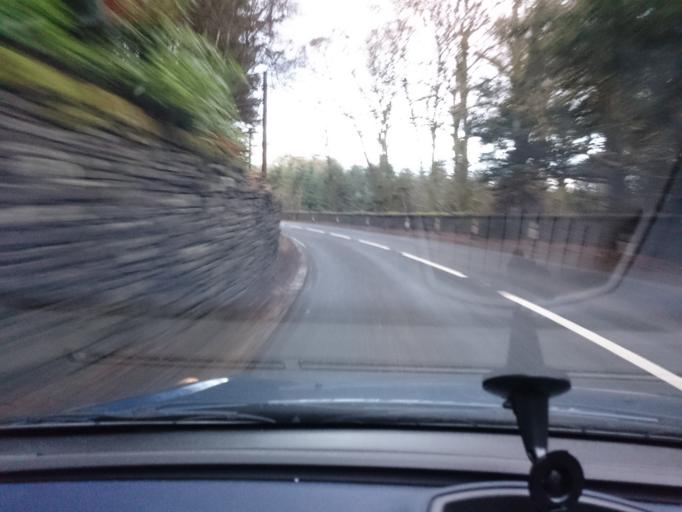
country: GB
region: Scotland
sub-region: Stirling
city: Doune
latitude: 56.2048
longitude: -4.1138
